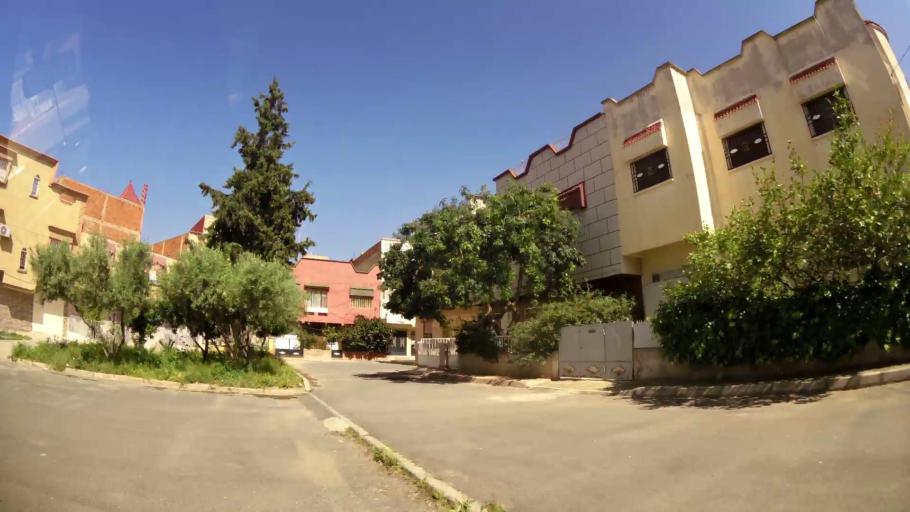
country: MA
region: Oriental
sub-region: Oujda-Angad
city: Oujda
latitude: 34.6951
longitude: -1.8730
